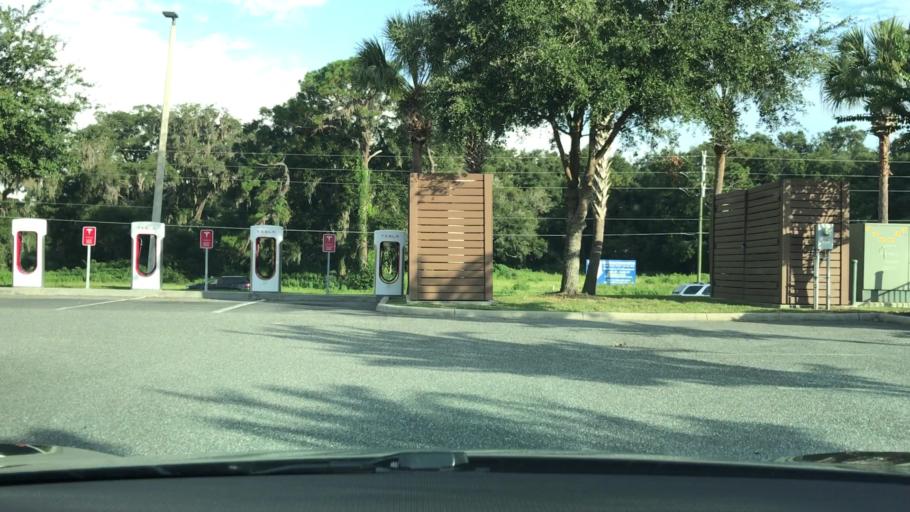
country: US
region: Florida
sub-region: Marion County
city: Ocala
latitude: 29.1409
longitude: -82.1938
